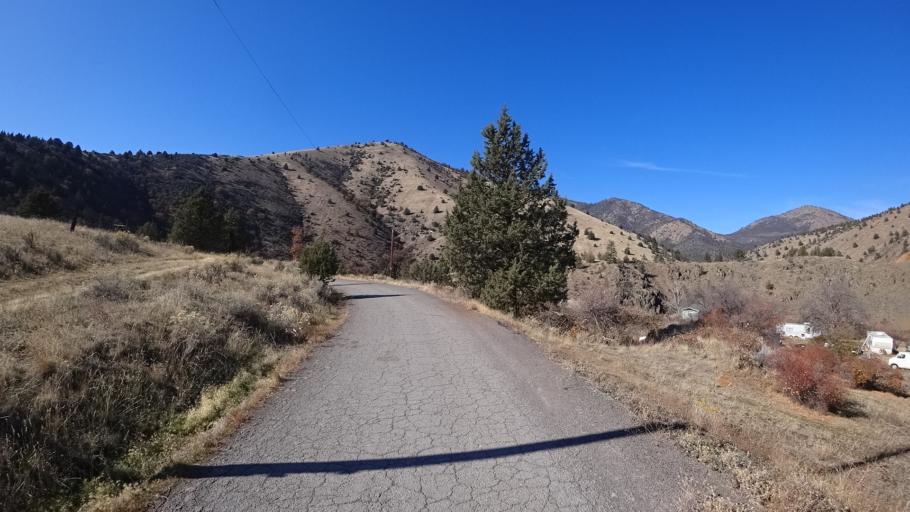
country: US
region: California
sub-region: Siskiyou County
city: Yreka
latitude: 41.7825
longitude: -122.5995
